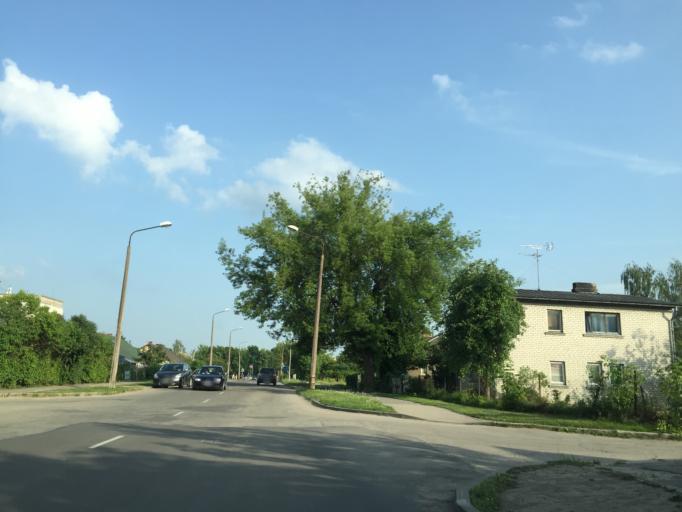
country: LV
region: Jelgava
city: Jelgava
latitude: 56.6604
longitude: 23.7051
